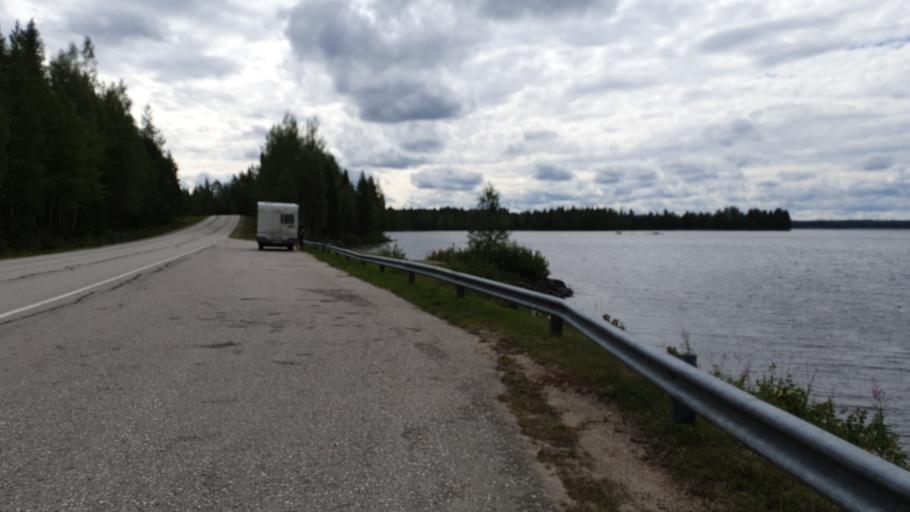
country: FI
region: Kainuu
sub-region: Kehys-Kainuu
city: Kuhmo
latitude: 64.4555
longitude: 29.7710
